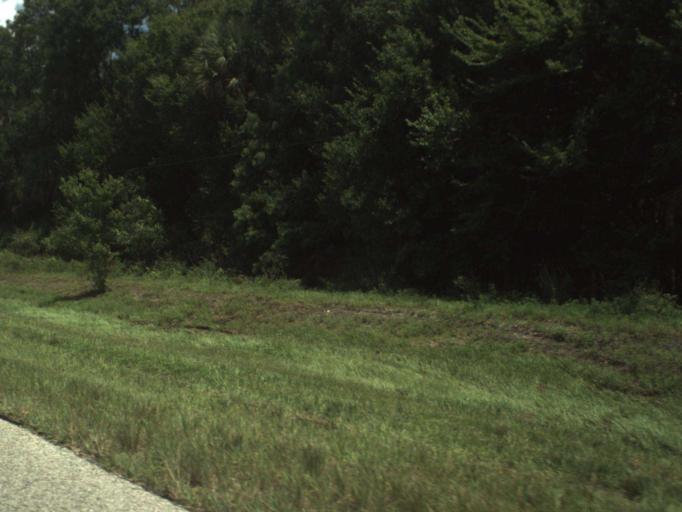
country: US
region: Florida
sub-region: Indian River County
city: Fellsmere
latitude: 27.6674
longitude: -80.8004
